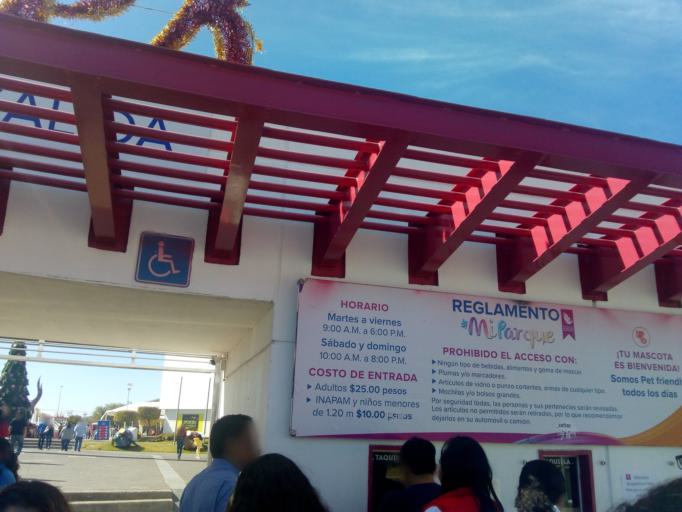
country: MX
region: Guanajuato
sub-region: Silao de la Victoria
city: Aguas Buenas
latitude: 20.9579
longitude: -101.3591
